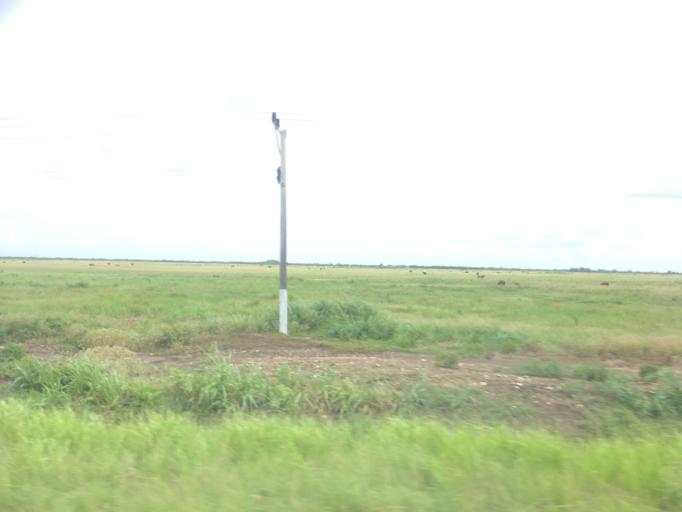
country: CU
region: Matanzas
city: Los Arabos
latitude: 22.7284
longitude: -80.7412
